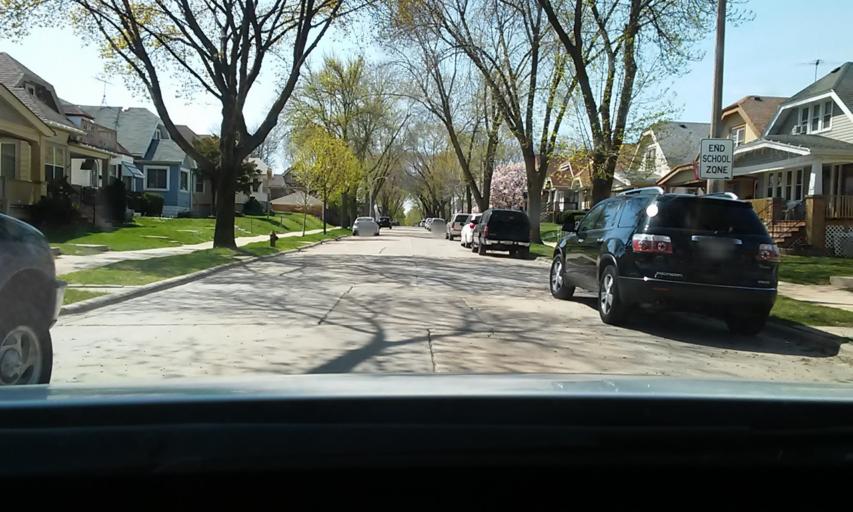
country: US
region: Wisconsin
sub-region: Milwaukee County
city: West Milwaukee
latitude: 43.0061
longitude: -87.9566
